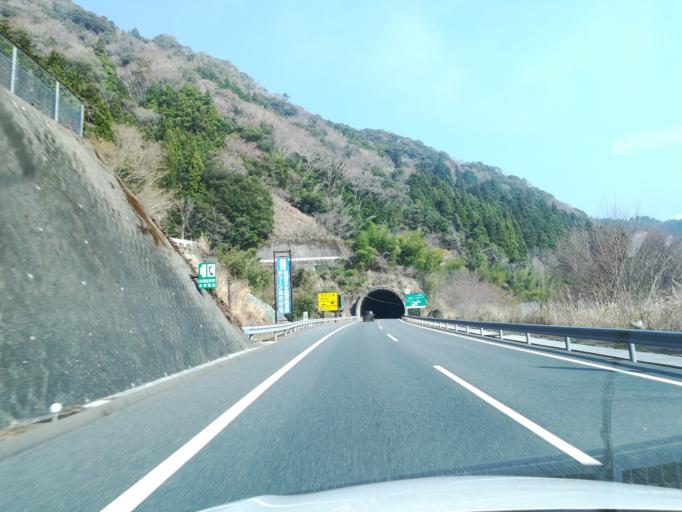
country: JP
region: Ehime
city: Kawanoecho
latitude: 33.7984
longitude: 133.6617
